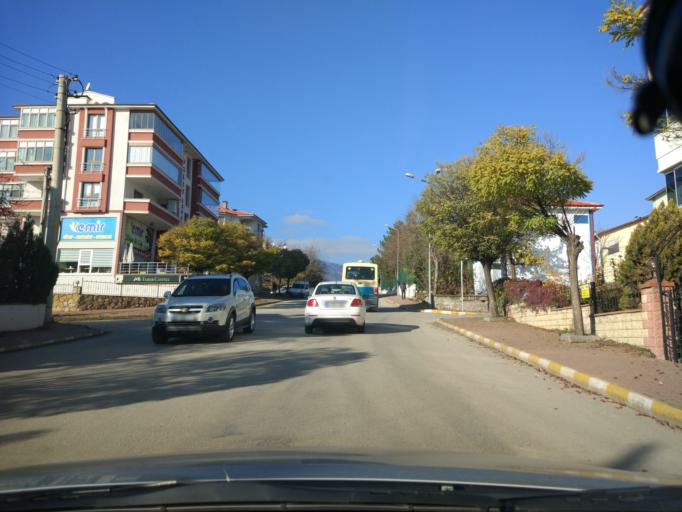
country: TR
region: Karabuk
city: Safranbolu
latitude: 41.2454
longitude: 32.6755
